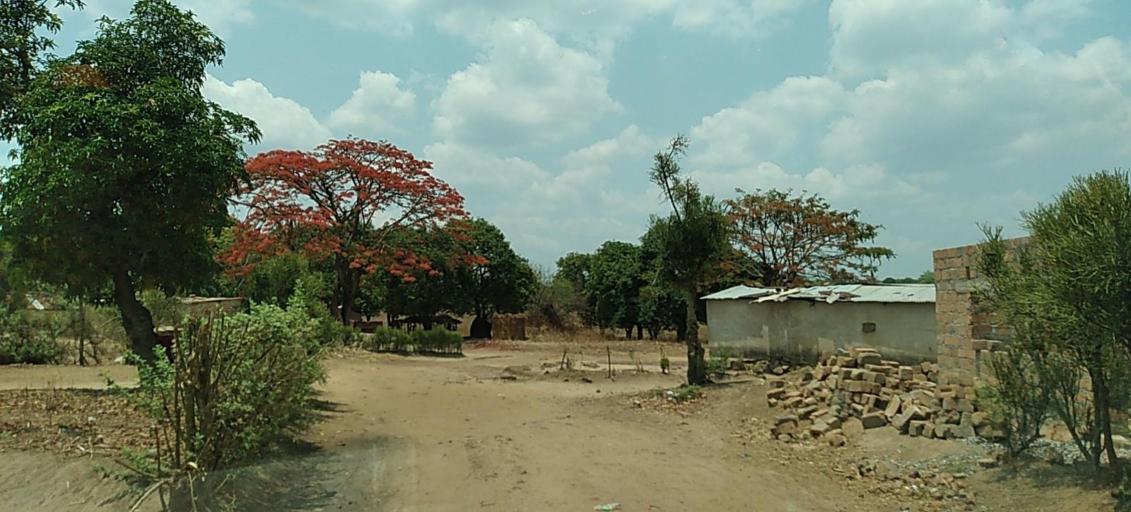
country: ZM
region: Copperbelt
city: Luanshya
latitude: -13.1207
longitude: 28.3074
